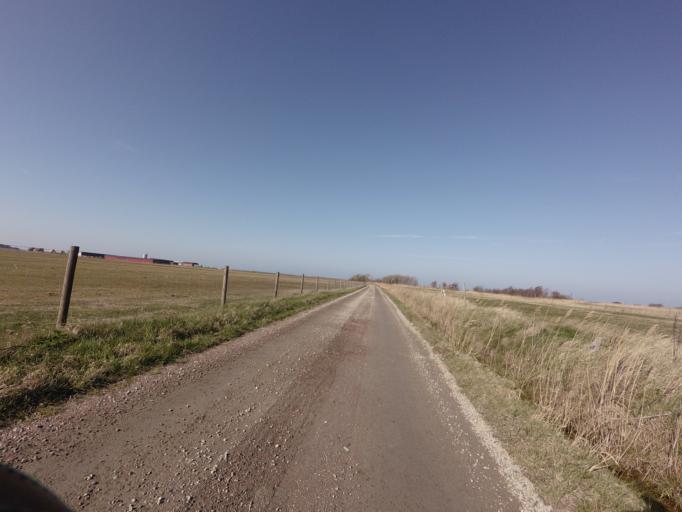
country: SE
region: Skane
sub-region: Vellinge Kommun
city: Skanor med Falsterbo
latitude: 55.4301
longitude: 12.8584
